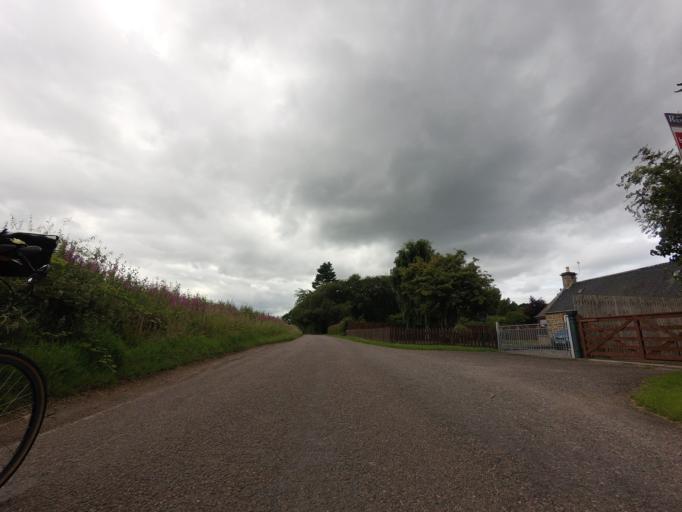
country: GB
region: Scotland
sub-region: Moray
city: Forres
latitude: 57.6150
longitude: -3.6826
